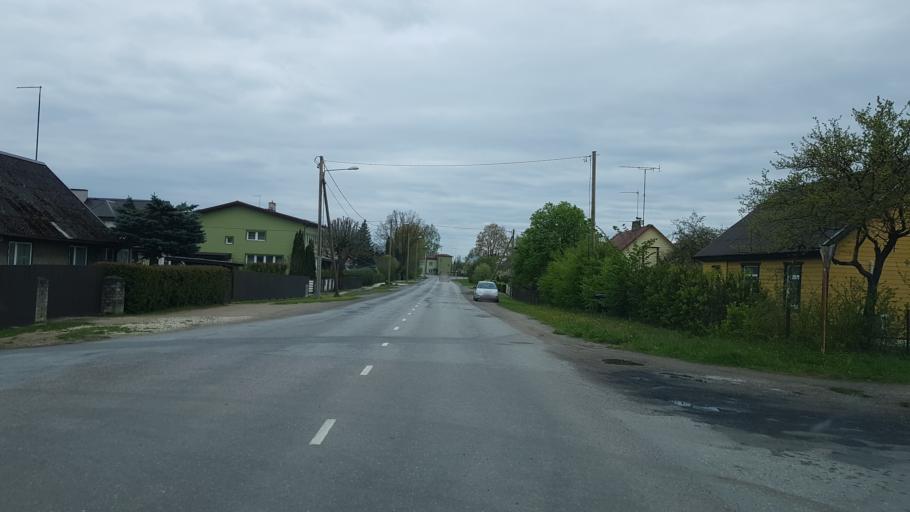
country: EE
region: Viljandimaa
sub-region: Viljandi linn
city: Viljandi
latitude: 58.3760
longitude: 25.6011
